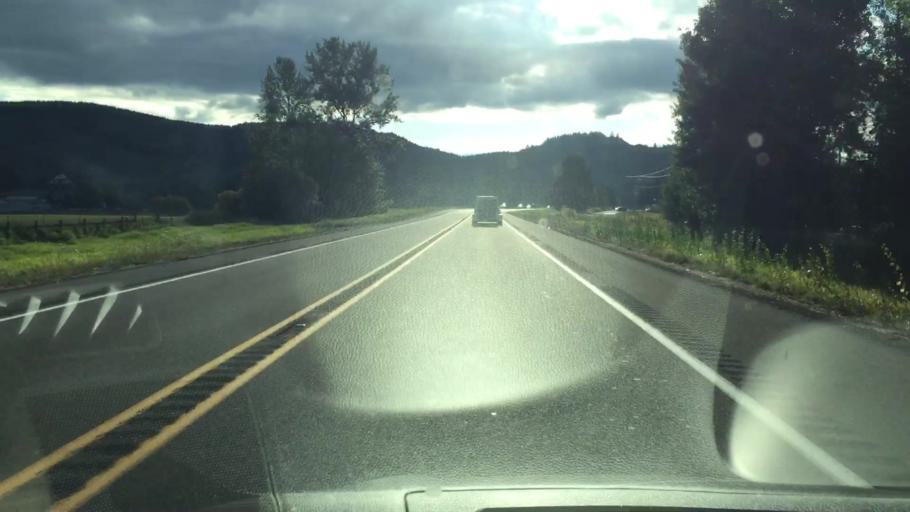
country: US
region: Washington
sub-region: Lewis County
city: Morton
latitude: 46.5327
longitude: -122.5225
